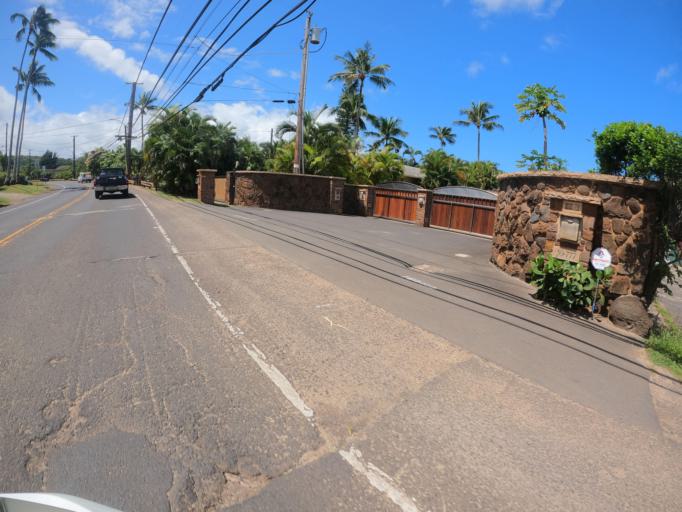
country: US
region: Hawaii
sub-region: Honolulu County
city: Pupukea
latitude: 21.6450
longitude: -158.0638
